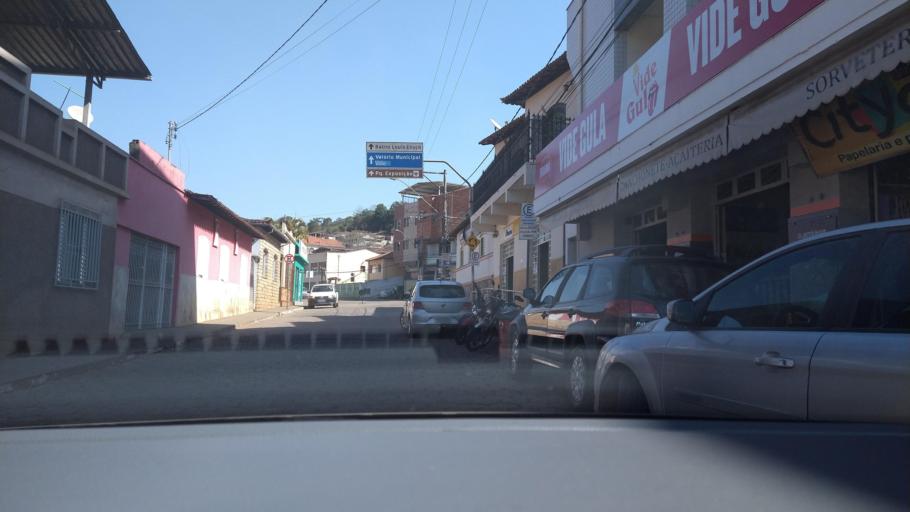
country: BR
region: Minas Gerais
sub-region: Rio Piracicaba
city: Rio Piracicaba
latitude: -19.9321
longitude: -43.1749
